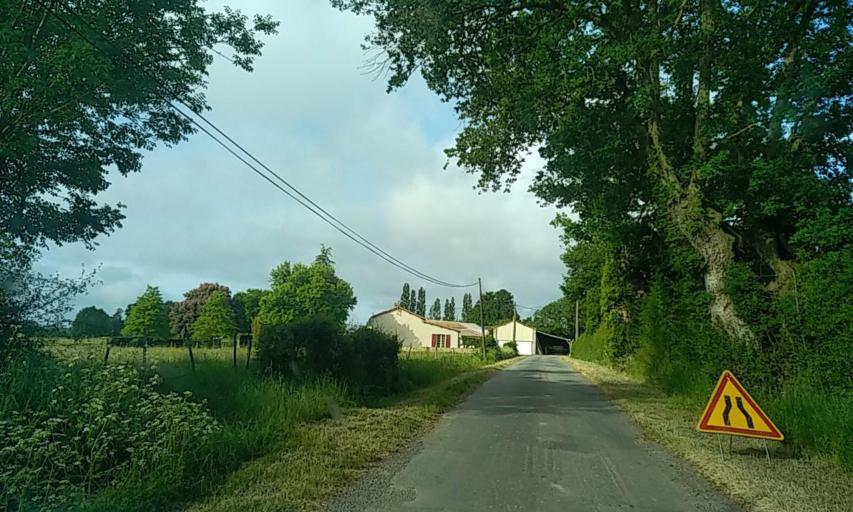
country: FR
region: Poitou-Charentes
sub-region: Departement des Deux-Sevres
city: Boisme
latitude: 46.7638
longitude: -0.4316
